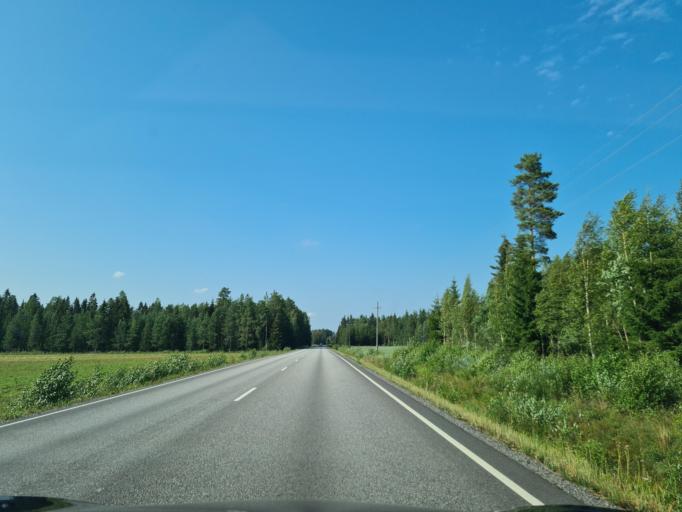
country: FI
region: Satakunta
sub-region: Pohjois-Satakunta
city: Kankaanpaeae
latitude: 61.9302
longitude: 22.5076
